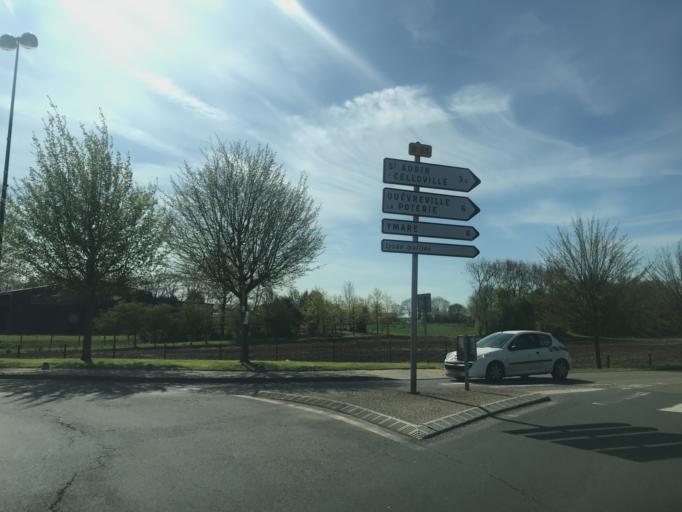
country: FR
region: Haute-Normandie
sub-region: Departement de la Seine-Maritime
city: Boos
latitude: 49.3989
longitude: 1.1742
